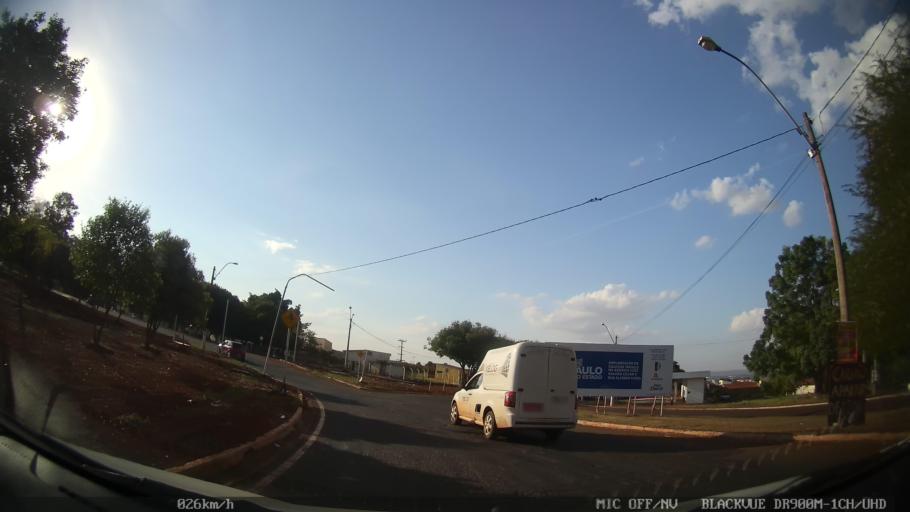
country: BR
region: Sao Paulo
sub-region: Ribeirao Preto
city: Ribeirao Preto
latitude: -21.1393
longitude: -47.8338
